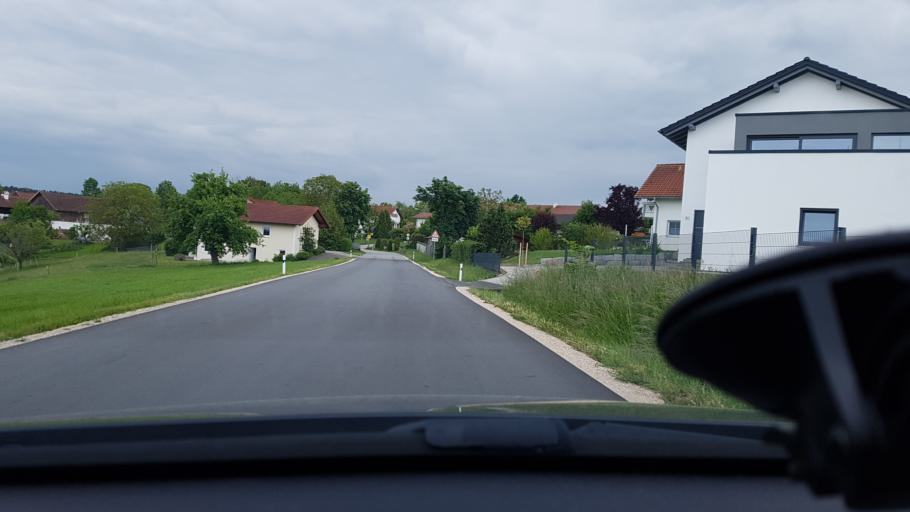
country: DE
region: Bavaria
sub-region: Lower Bavaria
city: Triftern
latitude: 48.3827
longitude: 13.0077
